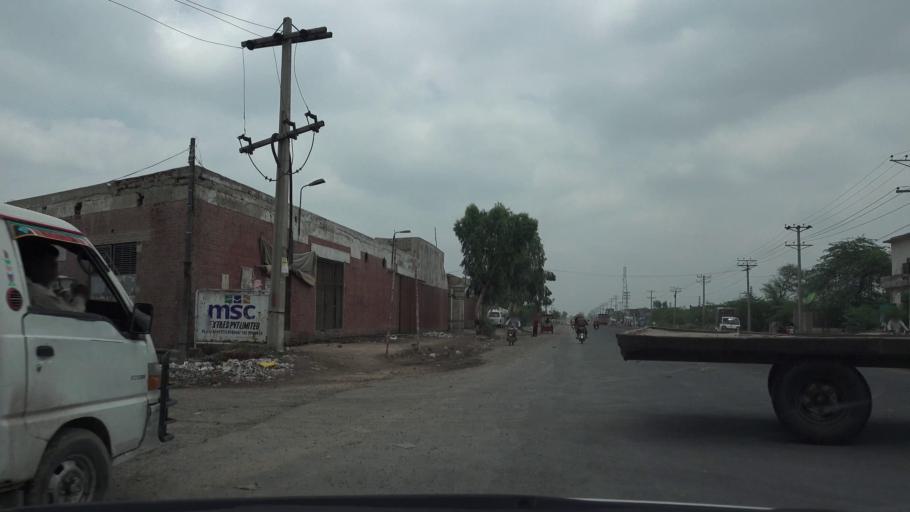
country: PK
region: Punjab
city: Faisalabad
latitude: 31.3932
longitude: 73.1811
